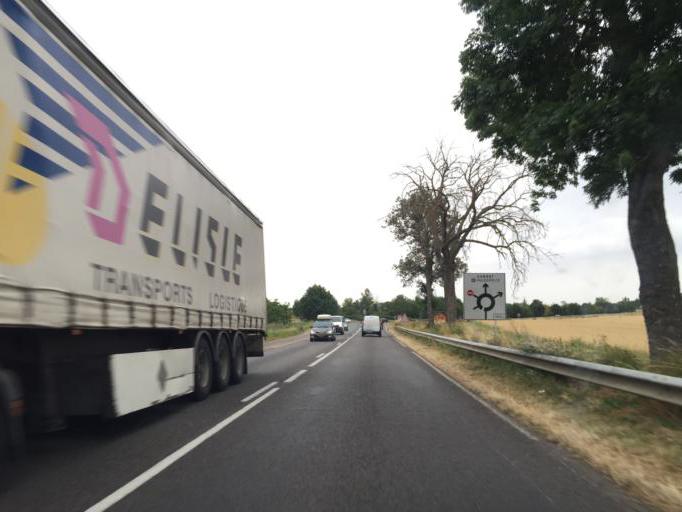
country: FR
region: Auvergne
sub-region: Departement de l'Allier
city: Gannat
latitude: 46.1171
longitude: 3.2022
